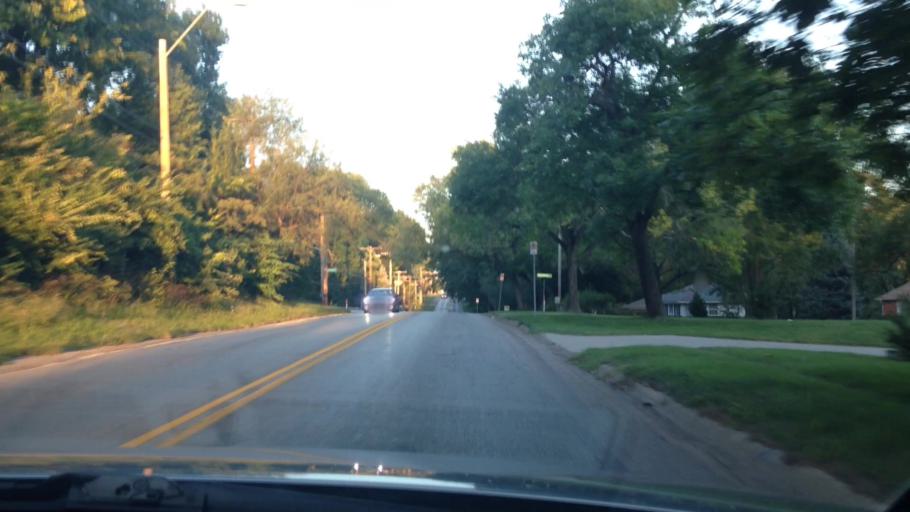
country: US
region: Missouri
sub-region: Jackson County
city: Grandview
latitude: 38.9243
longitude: -94.5426
